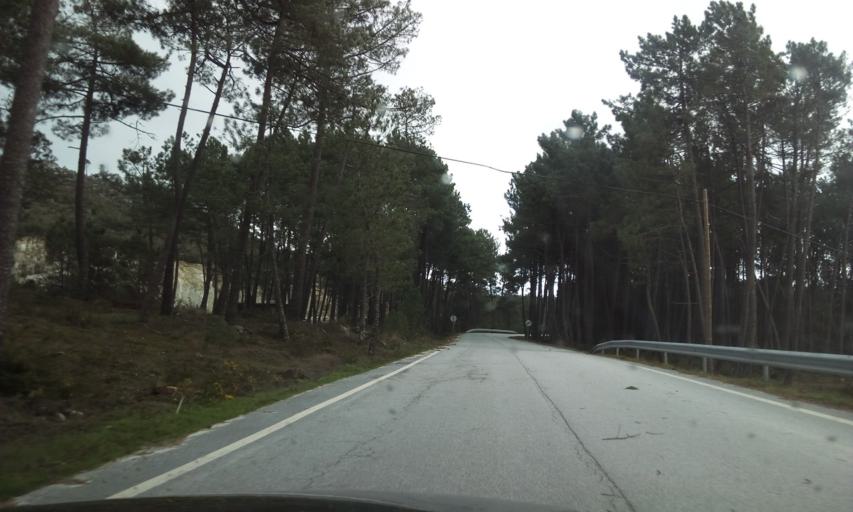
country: PT
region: Guarda
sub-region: Fornos de Algodres
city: Fornos de Algodres
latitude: 40.6328
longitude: -7.6104
